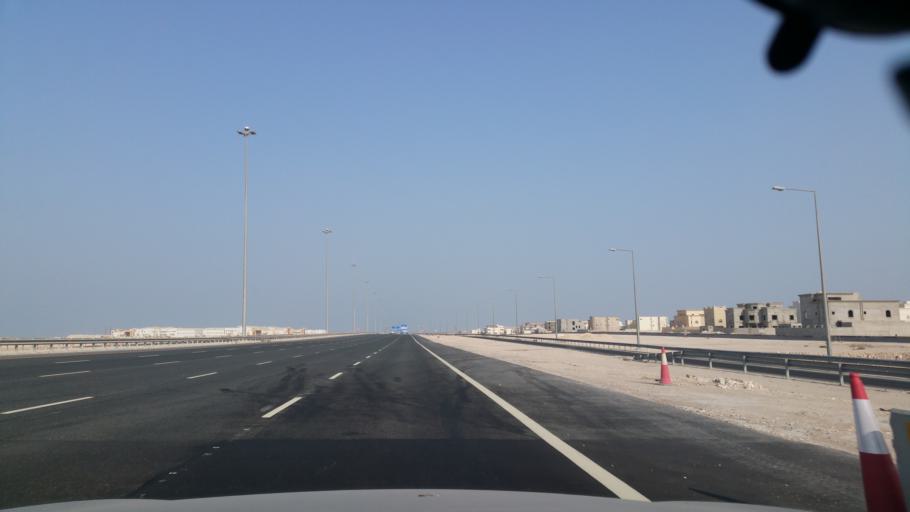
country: QA
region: Baladiyat Umm Salal
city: Umm Salal `Ali
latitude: 25.4567
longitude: 51.4523
